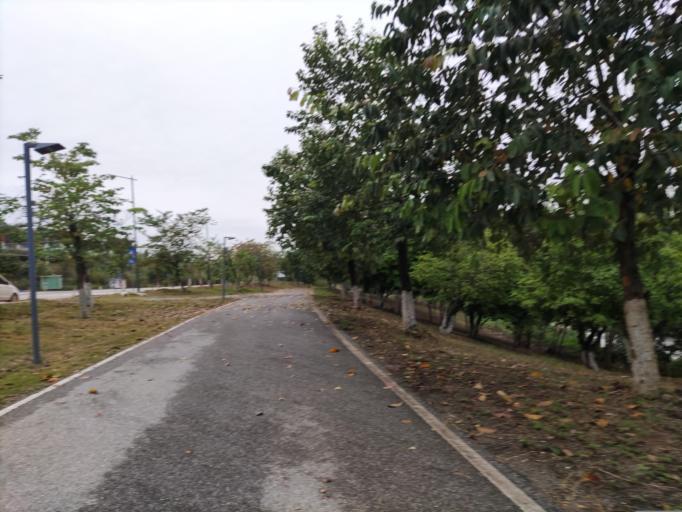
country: CN
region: Guangxi Zhuangzu Zizhiqu
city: Tianzhou
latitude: 23.7799
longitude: 106.7318
